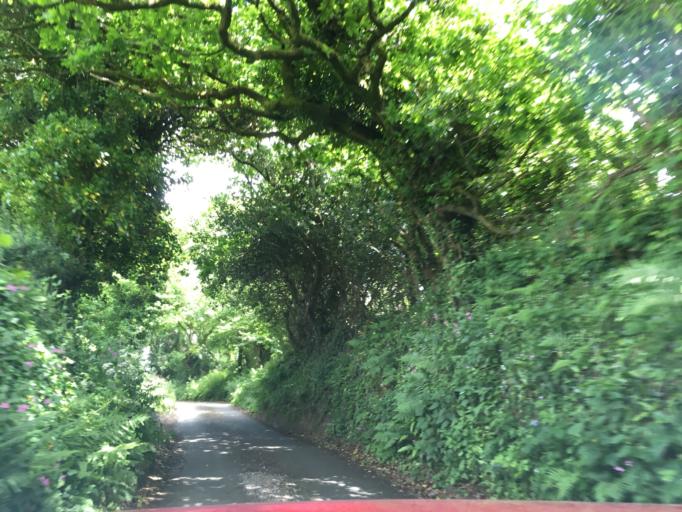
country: GB
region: England
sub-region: Devon
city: Totnes
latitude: 50.3769
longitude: -3.6900
